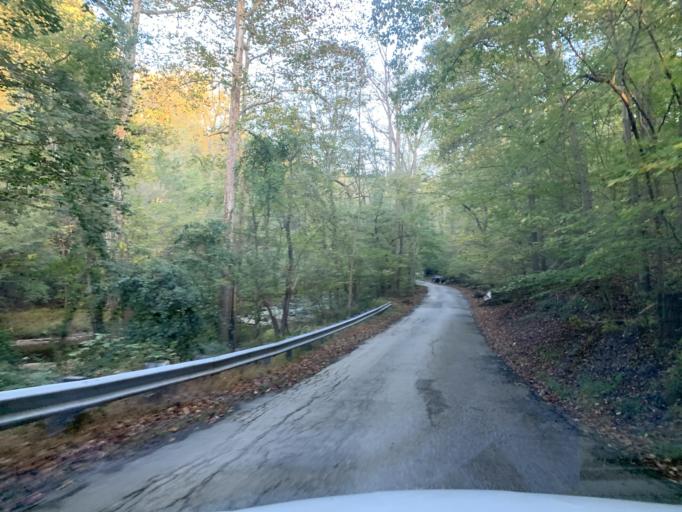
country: US
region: Maryland
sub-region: Harford County
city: Fallston
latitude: 39.5056
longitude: -76.4327
